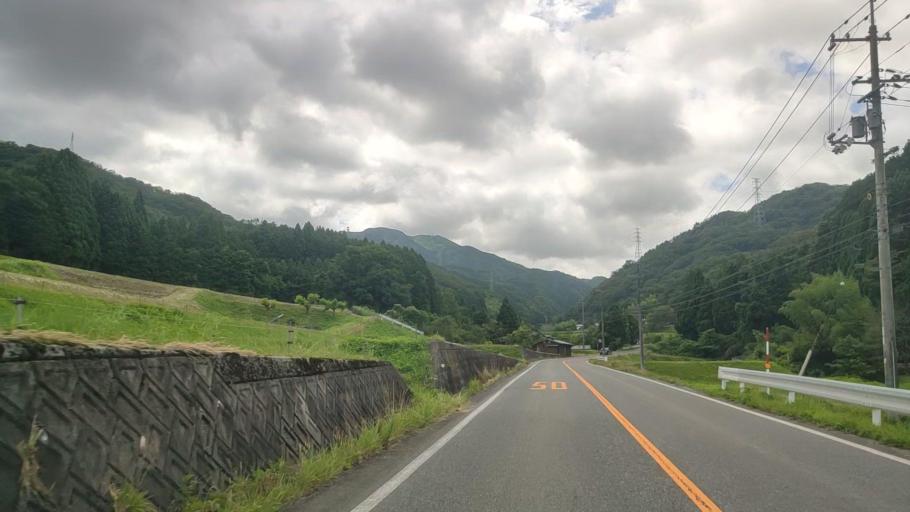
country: JP
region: Tottori
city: Yonago
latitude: 35.2906
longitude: 133.4217
